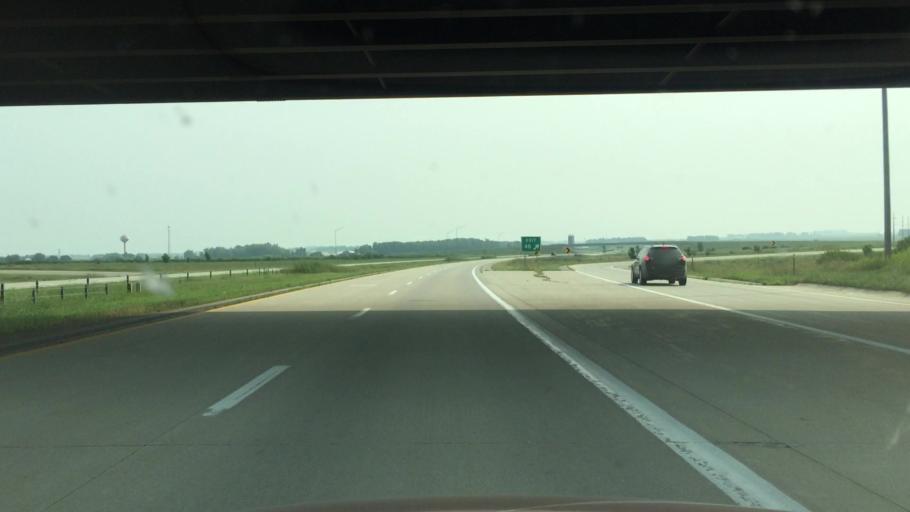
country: US
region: Iowa
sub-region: Osceola County
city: Sibley
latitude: 43.3821
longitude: -95.7508
